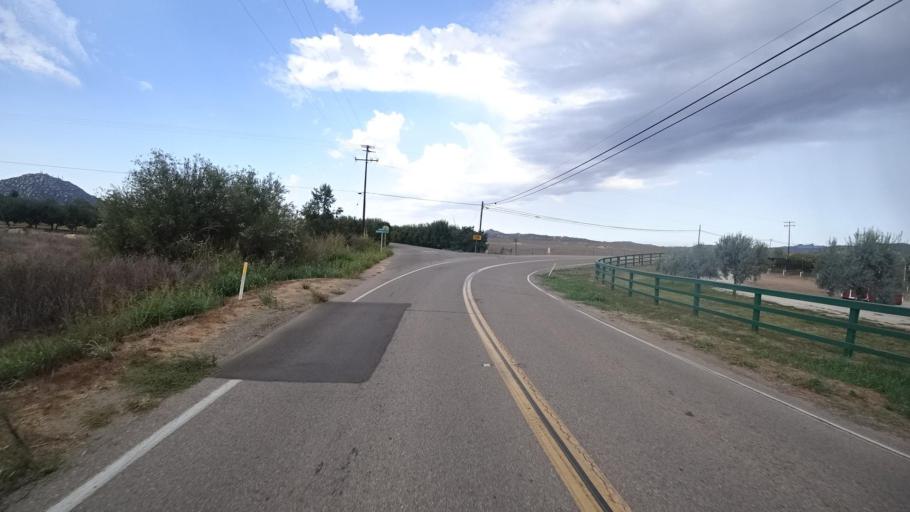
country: US
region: California
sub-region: San Diego County
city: San Pasqual
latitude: 33.0273
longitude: -116.9356
